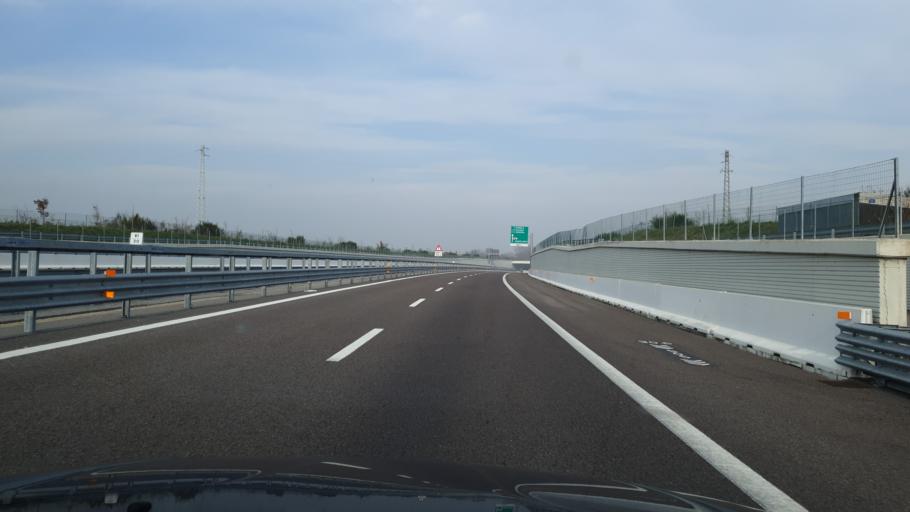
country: IT
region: Veneto
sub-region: Provincia di Vicenza
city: Agugliaro
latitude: 45.3236
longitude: 11.5738
